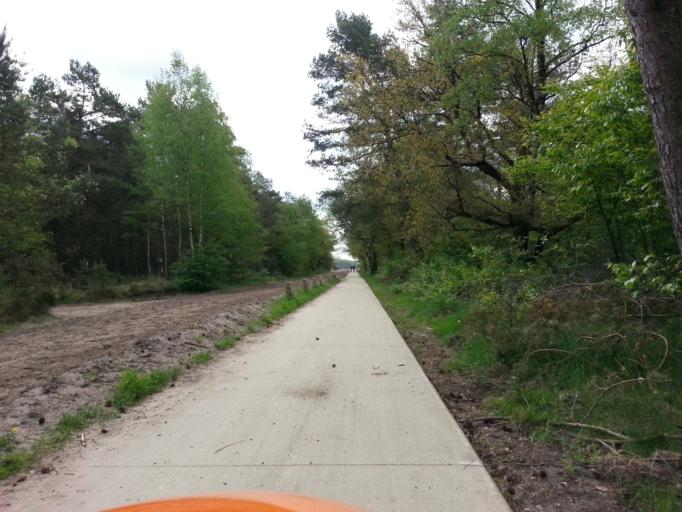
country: NL
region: Gelderland
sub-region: Gemeente Ede
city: Ede
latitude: 52.0613
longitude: 5.6959
